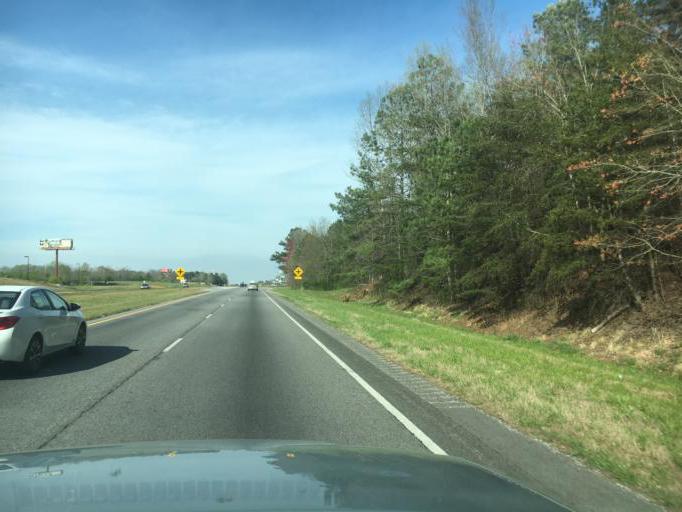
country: US
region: Georgia
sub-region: Banks County
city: Alto
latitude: 34.4781
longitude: -83.5891
